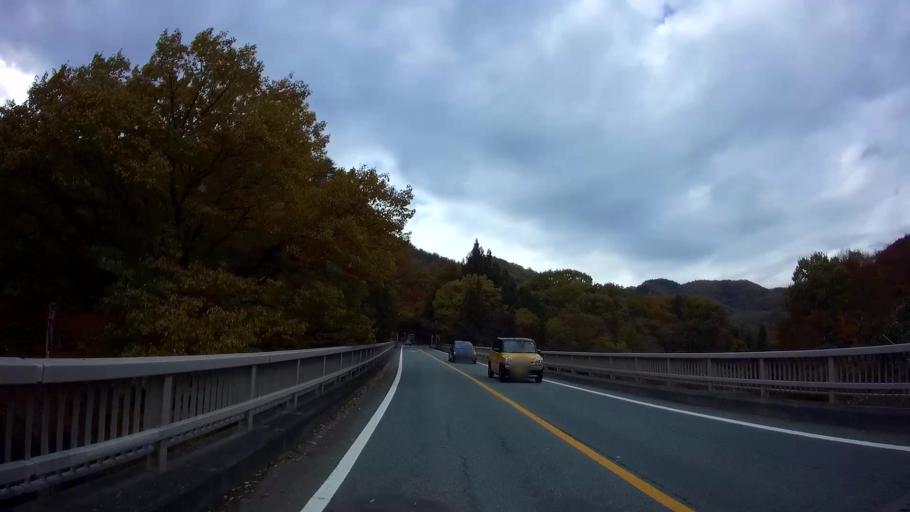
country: JP
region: Gunma
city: Nakanojomachi
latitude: 36.5688
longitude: 138.6341
